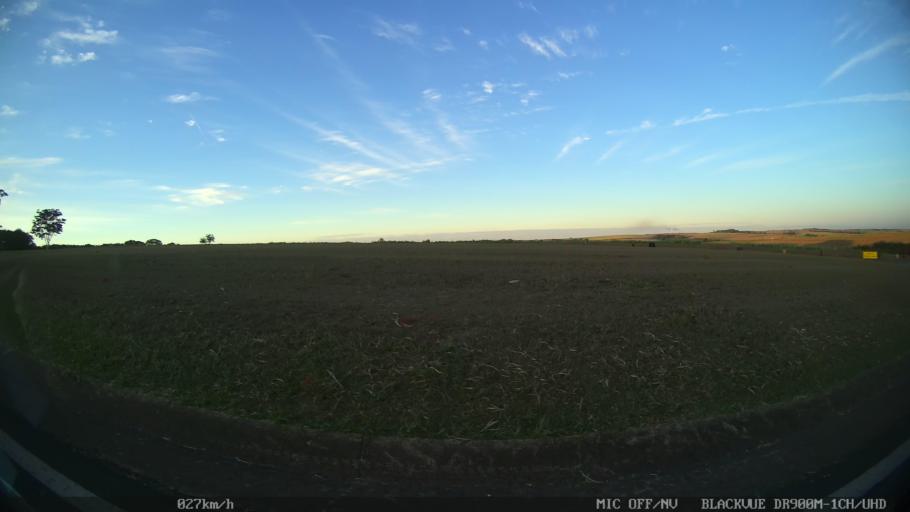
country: BR
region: Sao Paulo
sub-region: Pindorama
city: Pindorama
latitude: -21.2321
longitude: -48.9081
